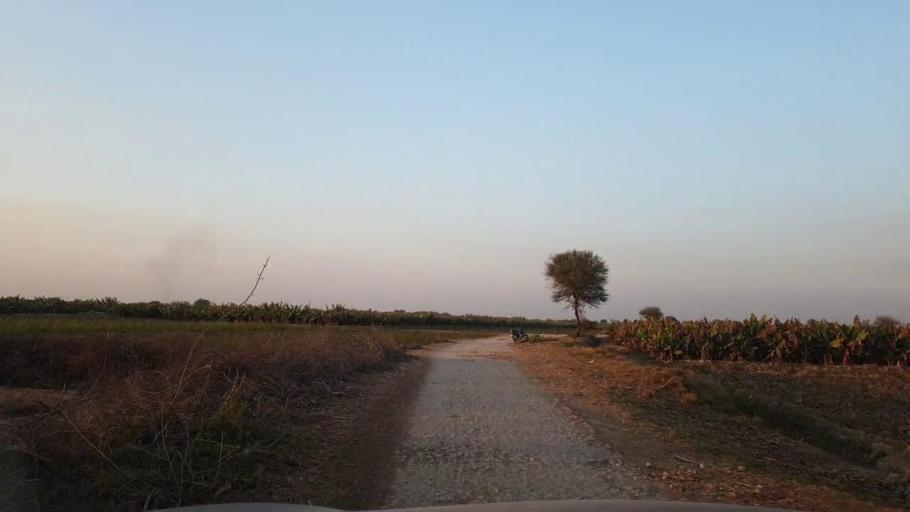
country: PK
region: Sindh
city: Berani
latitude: 25.6642
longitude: 68.7707
